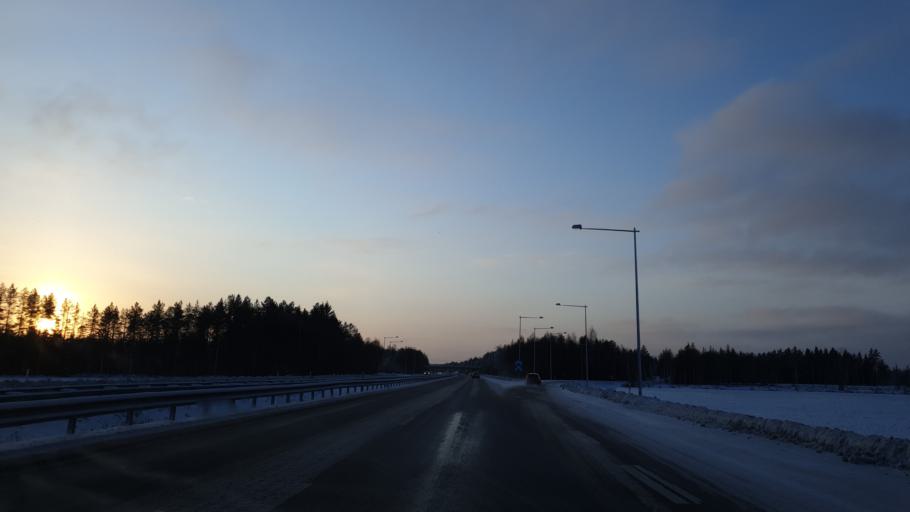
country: SE
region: Vaesterbotten
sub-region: Umea Kommun
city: Roback
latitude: 63.7895
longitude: 20.2095
